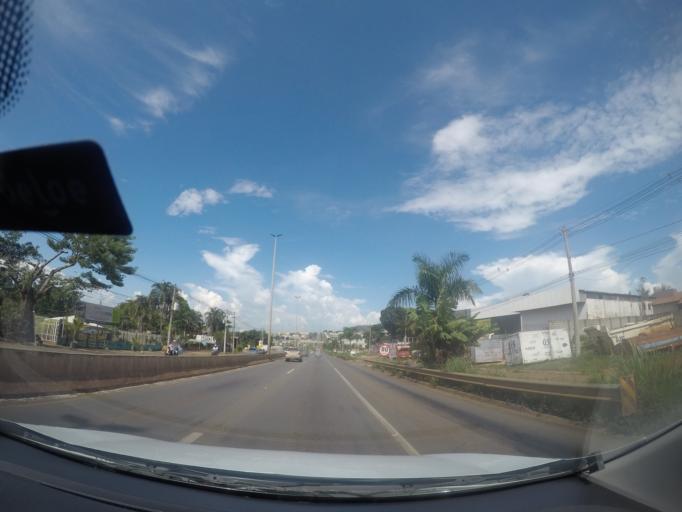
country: BR
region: Goias
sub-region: Goiania
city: Goiania
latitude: -16.6593
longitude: -49.3635
